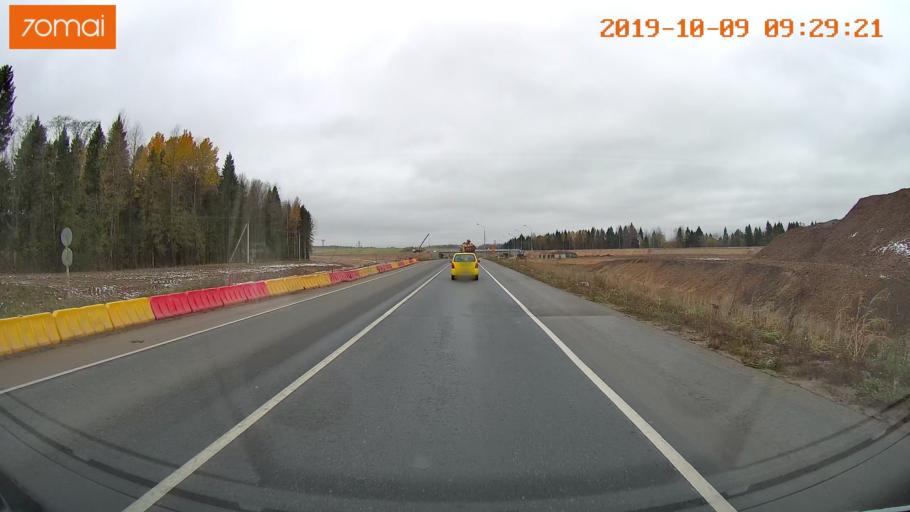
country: RU
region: Vologda
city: Vologda
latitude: 59.1312
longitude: 39.9586
